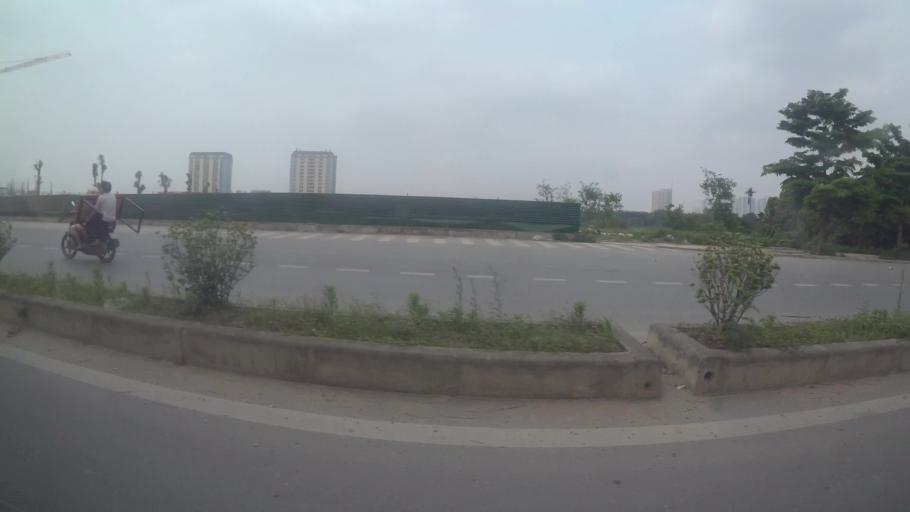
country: VN
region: Ha Noi
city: Cau Dien
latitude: 21.0367
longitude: 105.7494
